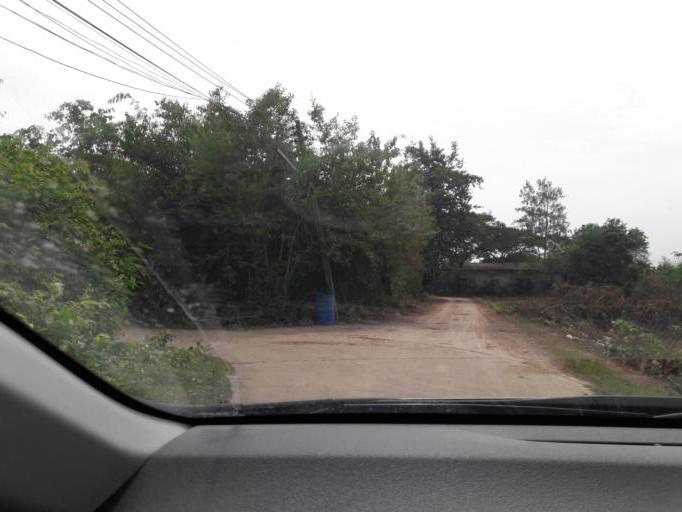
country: TH
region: Ratchaburi
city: Ratchaburi
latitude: 13.5188
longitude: 99.7955
